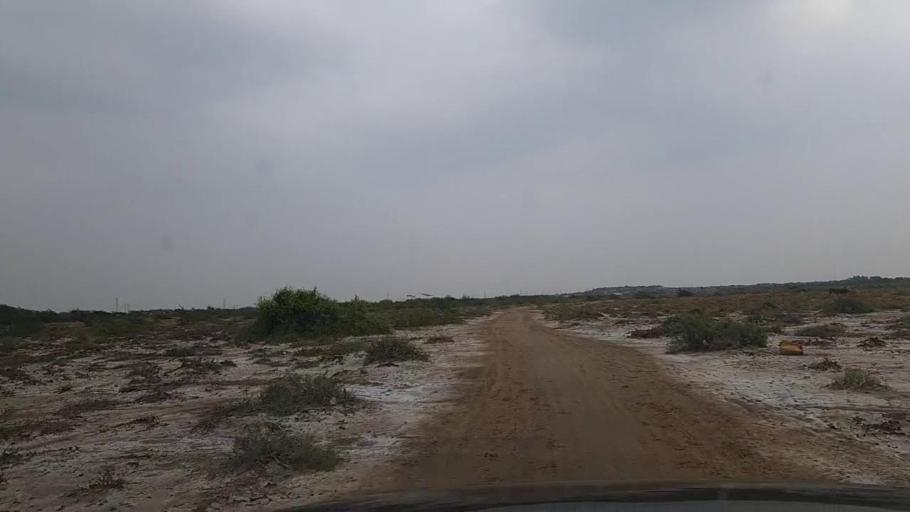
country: PK
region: Sindh
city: Thatta
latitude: 24.8186
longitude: 67.8263
